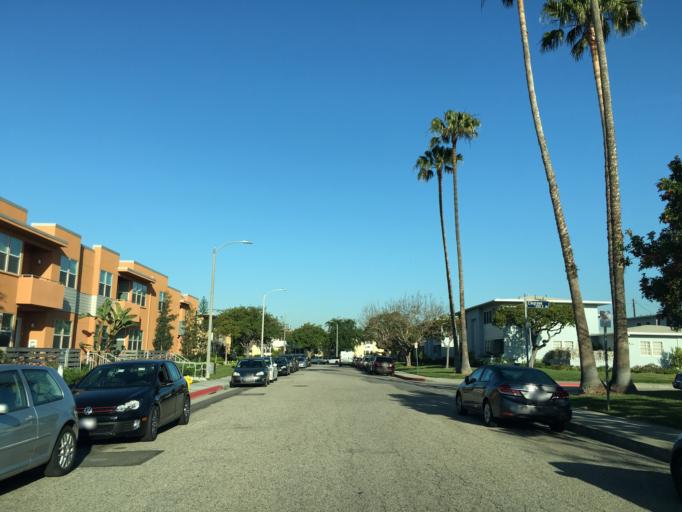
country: US
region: California
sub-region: Los Angeles County
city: Marina del Rey
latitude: 33.9998
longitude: -118.4594
